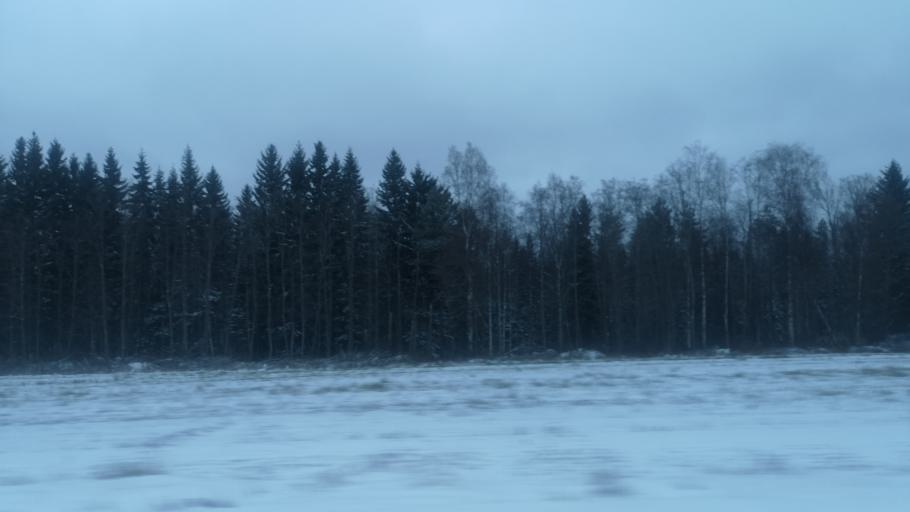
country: FI
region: Southern Savonia
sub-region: Savonlinna
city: Enonkoski
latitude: 62.0722
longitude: 28.7251
